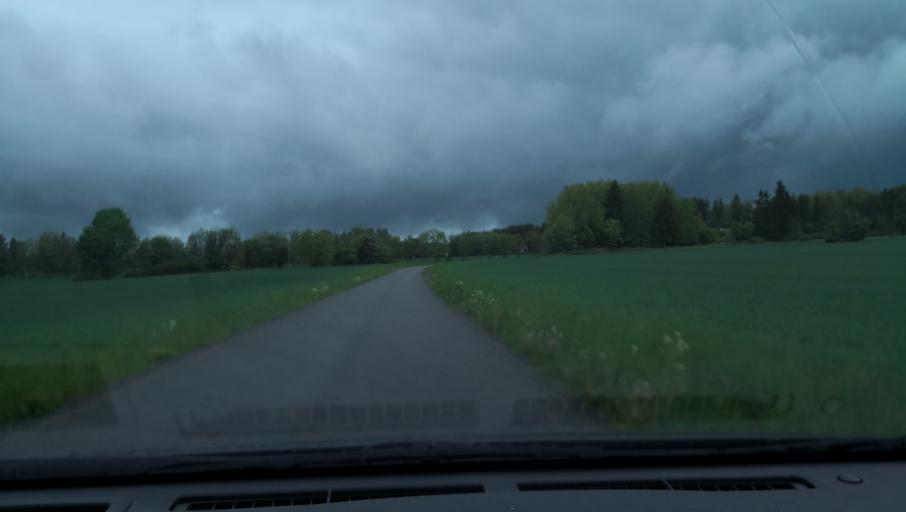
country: SE
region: Uppsala
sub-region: Enkopings Kommun
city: Orsundsbro
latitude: 59.8056
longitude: 17.3782
